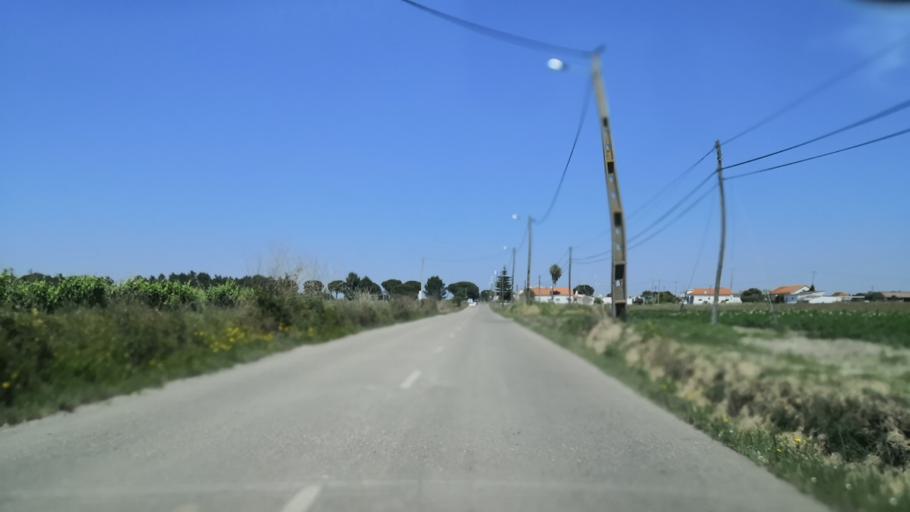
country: PT
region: Santarem
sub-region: Benavente
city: Poceirao
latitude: 38.6721
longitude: -8.7353
